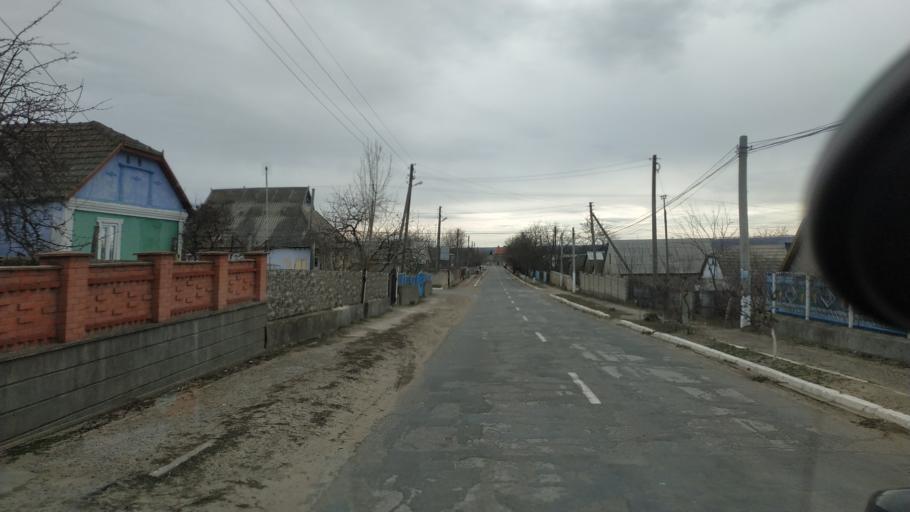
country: MD
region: Telenesti
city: Cocieri
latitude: 47.3015
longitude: 29.1138
